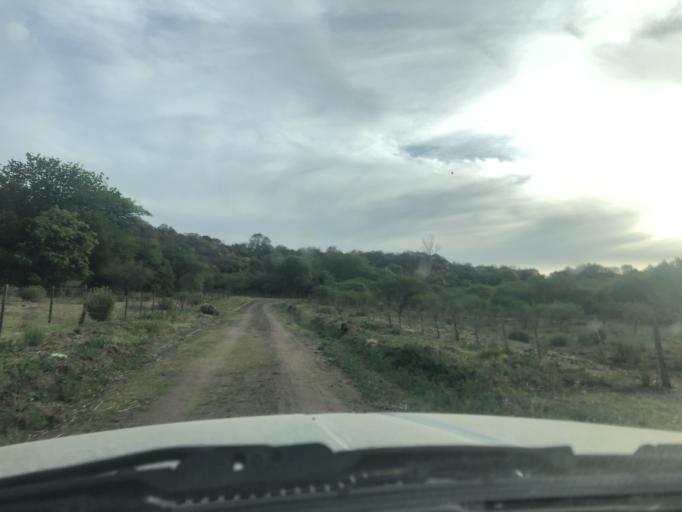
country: AR
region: Cordoba
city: La Granja
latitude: -31.0130
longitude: -64.2476
